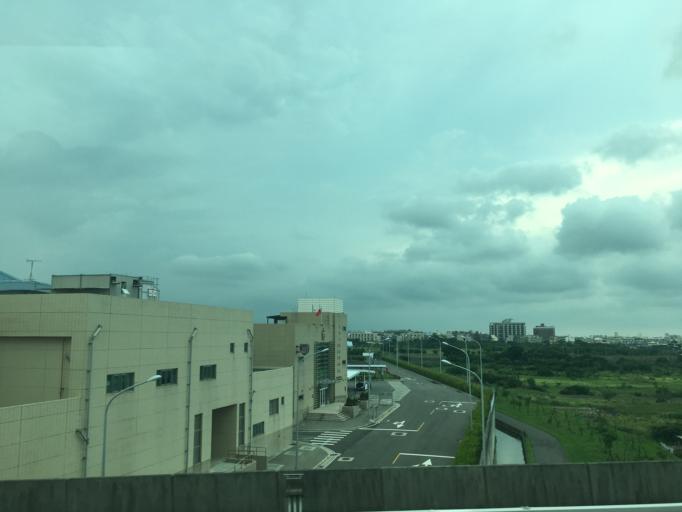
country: TW
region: Taiwan
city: Taoyuan City
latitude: 25.0853
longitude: 121.2685
